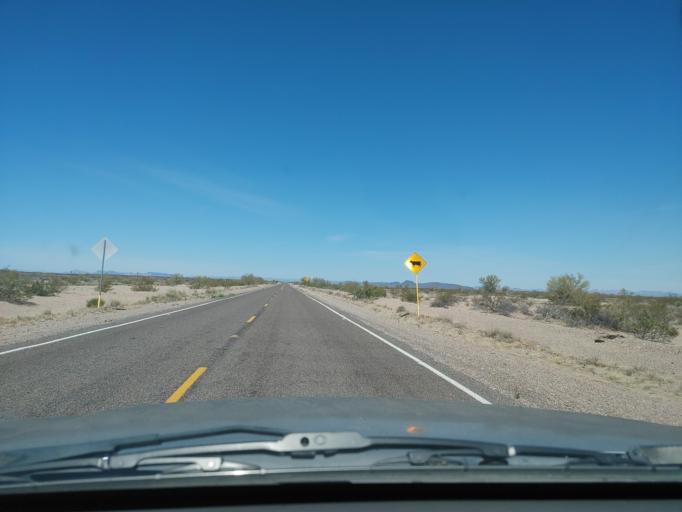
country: US
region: Arizona
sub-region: Maricopa County
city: Gila Bend
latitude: 32.8890
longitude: -113.2388
